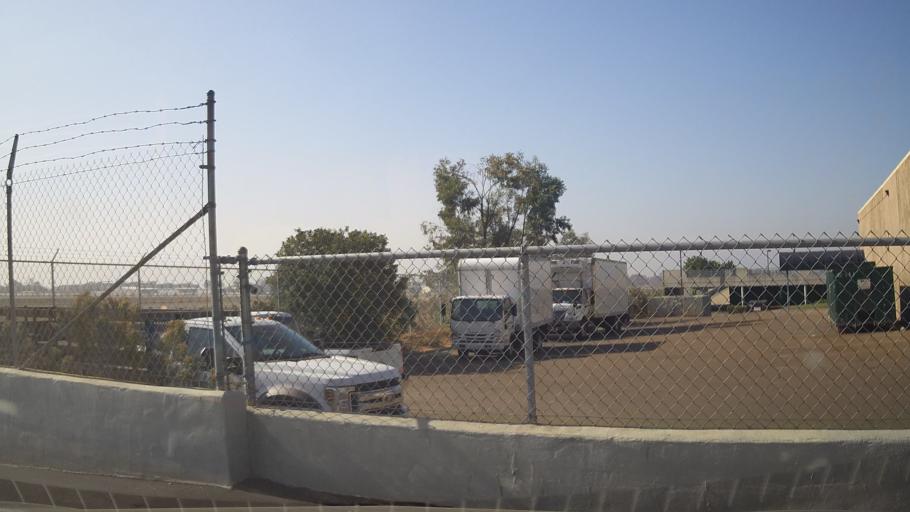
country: US
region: California
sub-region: San Diego County
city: San Diego
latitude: 32.8192
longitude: -117.1376
